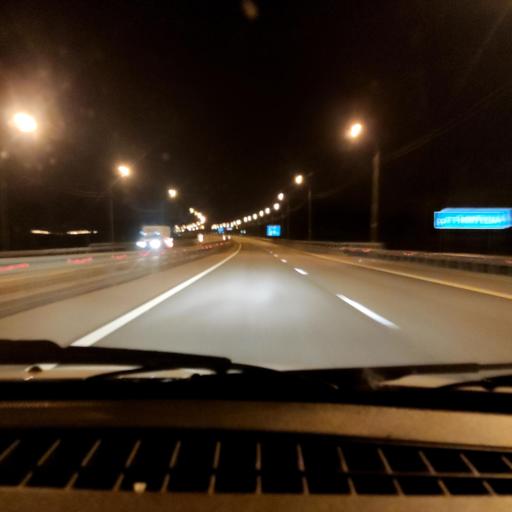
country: RU
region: Lipetsk
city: Zadonsk
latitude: 52.3243
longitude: 39.0278
